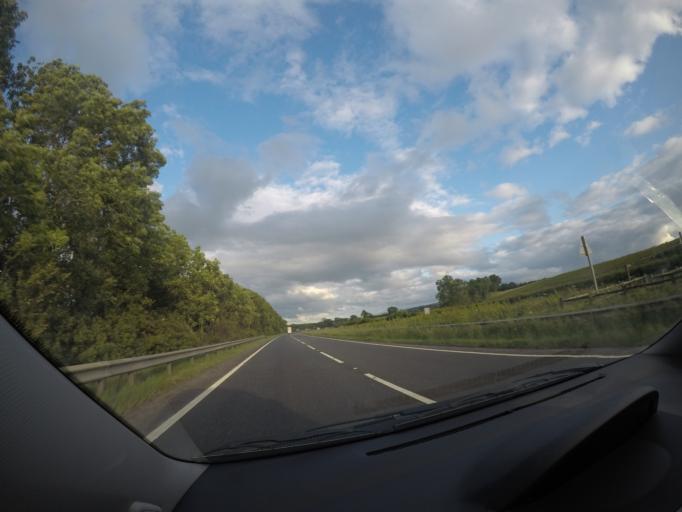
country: GB
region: England
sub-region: County Durham
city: Rokeby
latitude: 54.5031
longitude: -1.8414
